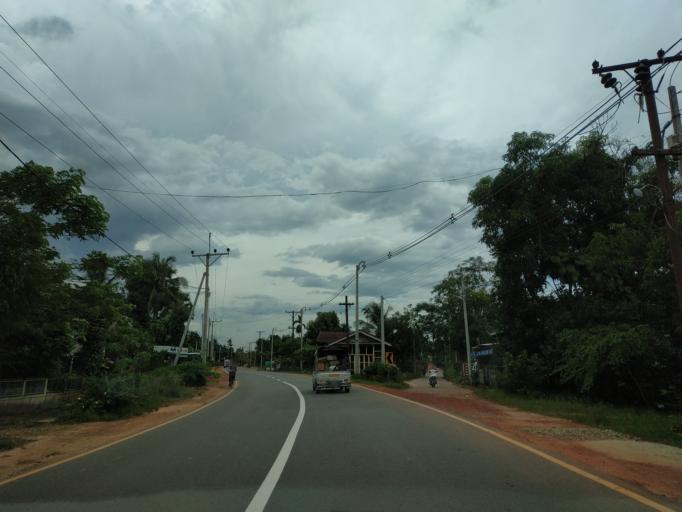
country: MM
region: Tanintharyi
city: Dawei
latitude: 14.0150
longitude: 98.2263
